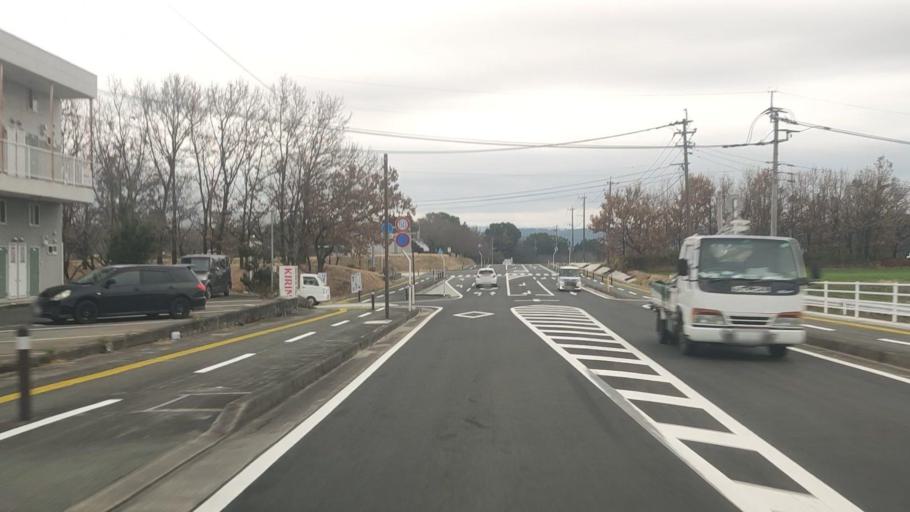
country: JP
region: Kumamoto
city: Ozu
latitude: 32.8746
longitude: 130.8941
